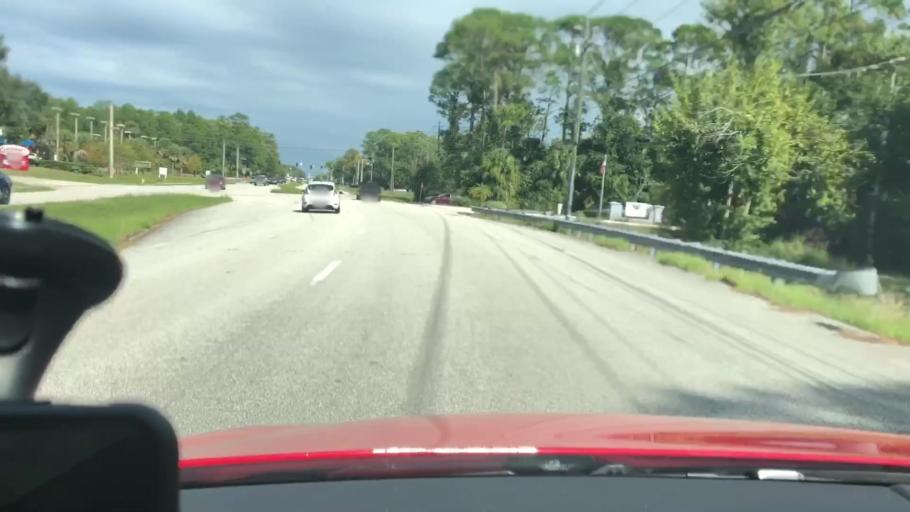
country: US
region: Florida
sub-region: Volusia County
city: Holly Hill
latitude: 29.2095
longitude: -81.0717
